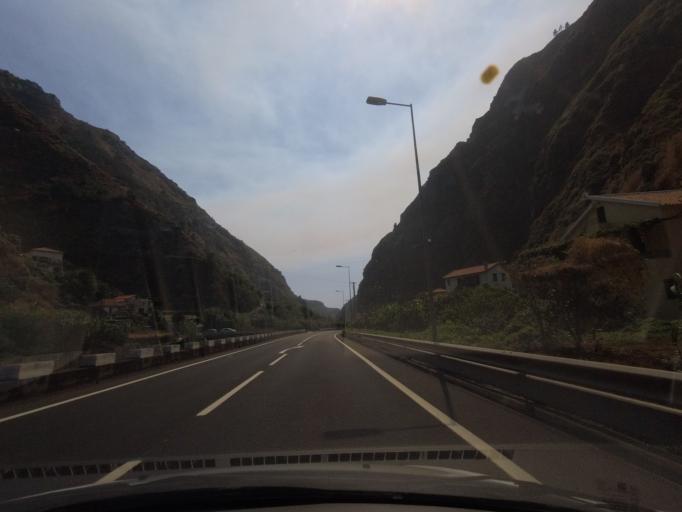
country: PT
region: Madeira
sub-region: Ribeira Brava
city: Campanario
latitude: 32.6982
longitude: -17.0422
